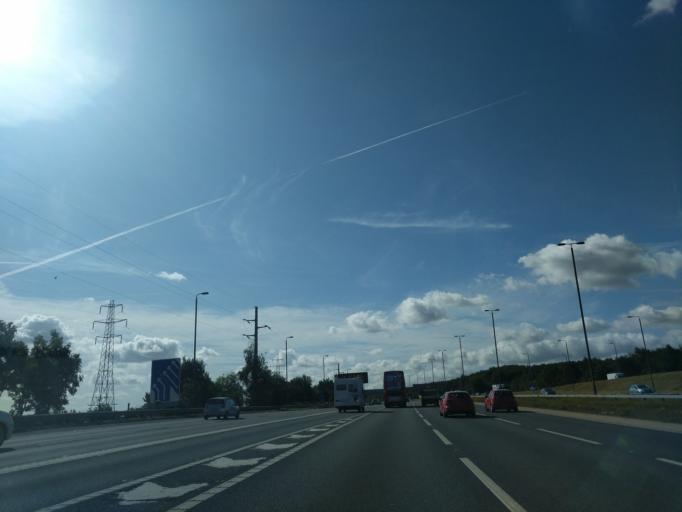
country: GB
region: England
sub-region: City and Borough of Leeds
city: Lofthouse
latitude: 53.7535
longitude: -1.5146
